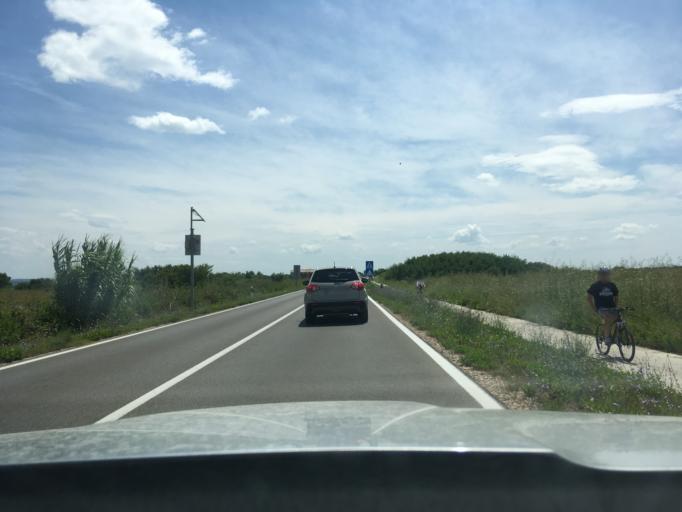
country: HR
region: Zadarska
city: Nin
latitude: 44.2521
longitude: 15.1607
